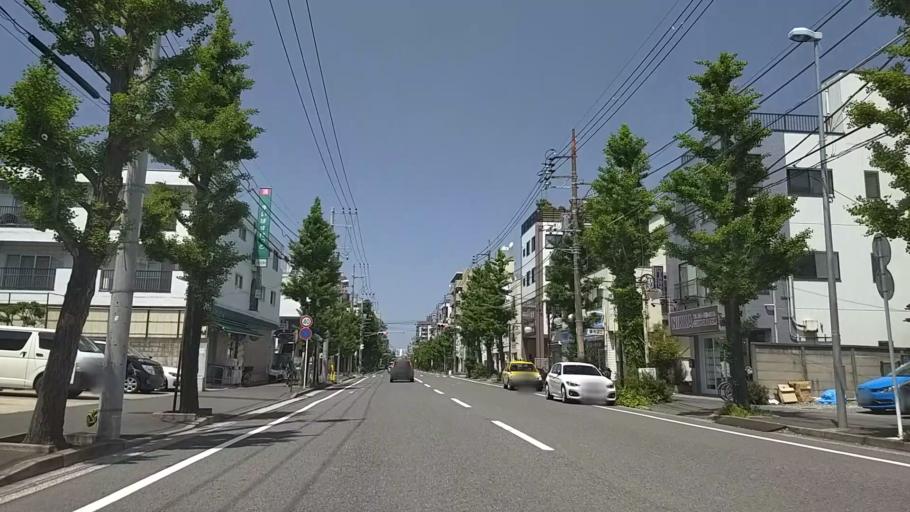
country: JP
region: Kanagawa
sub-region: Kawasaki-shi
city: Kawasaki
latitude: 35.5145
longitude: 139.7149
